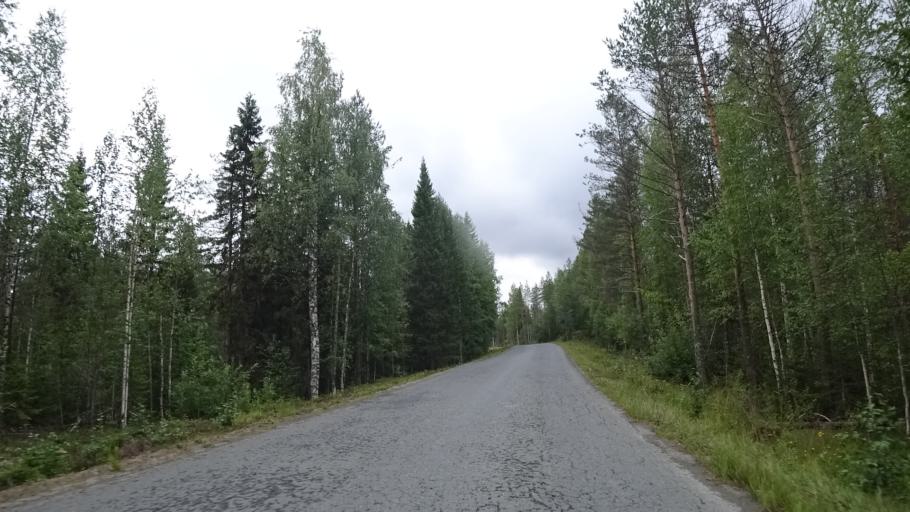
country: FI
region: North Karelia
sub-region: Joensuu
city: Ilomantsi
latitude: 62.9803
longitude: 31.2825
